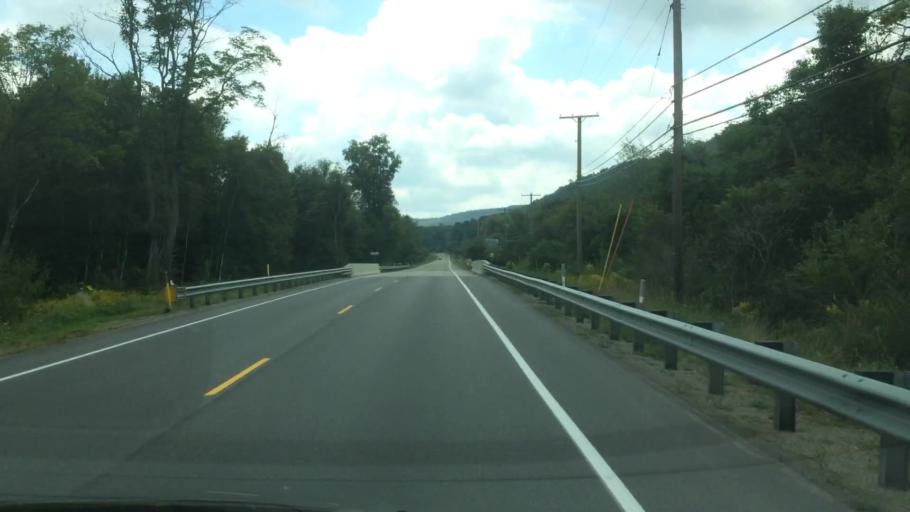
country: US
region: Pennsylvania
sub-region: McKean County
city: Bradford
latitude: 41.8990
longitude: -78.6098
